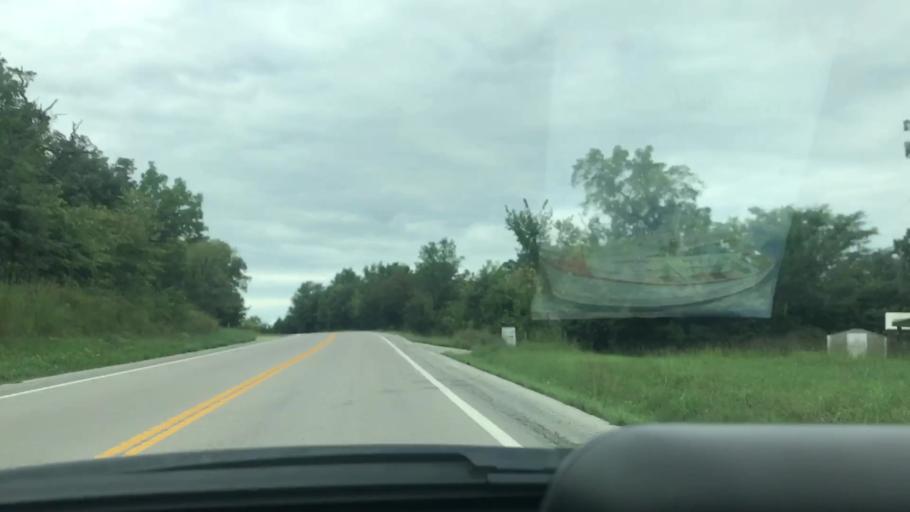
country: US
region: Missouri
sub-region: Benton County
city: Warsaw
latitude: 38.1683
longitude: -93.3097
